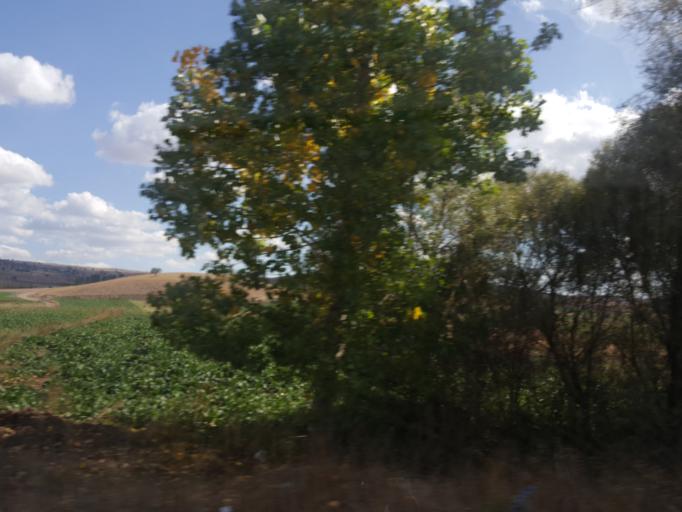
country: TR
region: Tokat
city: Camlibel
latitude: 40.1951
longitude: 36.4617
